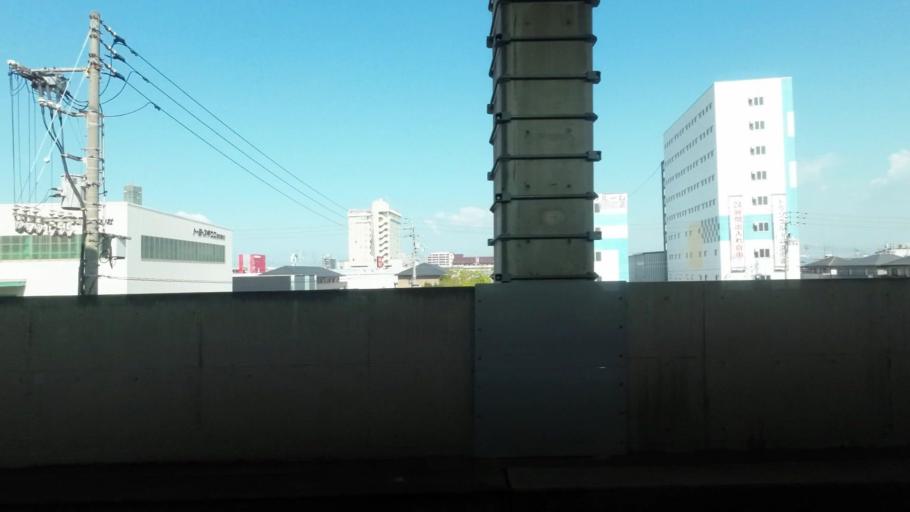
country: JP
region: Kagawa
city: Sakaidecho
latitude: 34.3120
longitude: 133.8175
